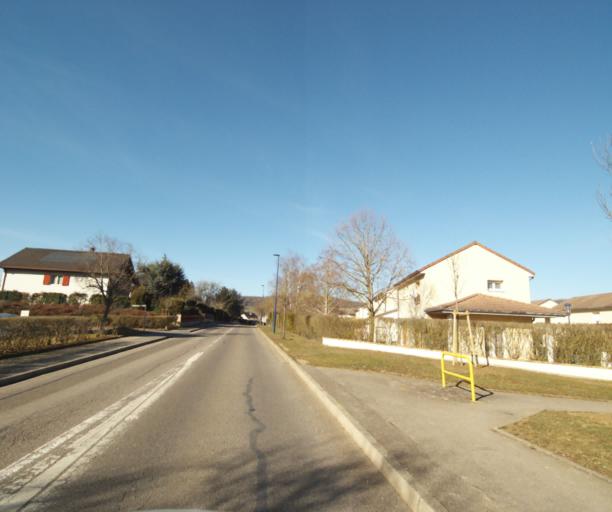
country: FR
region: Lorraine
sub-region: Departement de Meurthe-et-Moselle
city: Ludres
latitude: 48.6163
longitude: 6.1724
